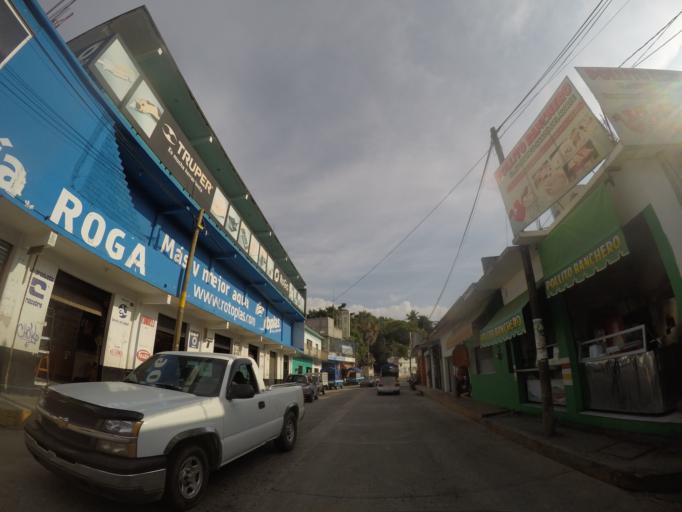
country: MX
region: Oaxaca
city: San Pedro Pochutla
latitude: 15.7481
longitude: -96.4670
